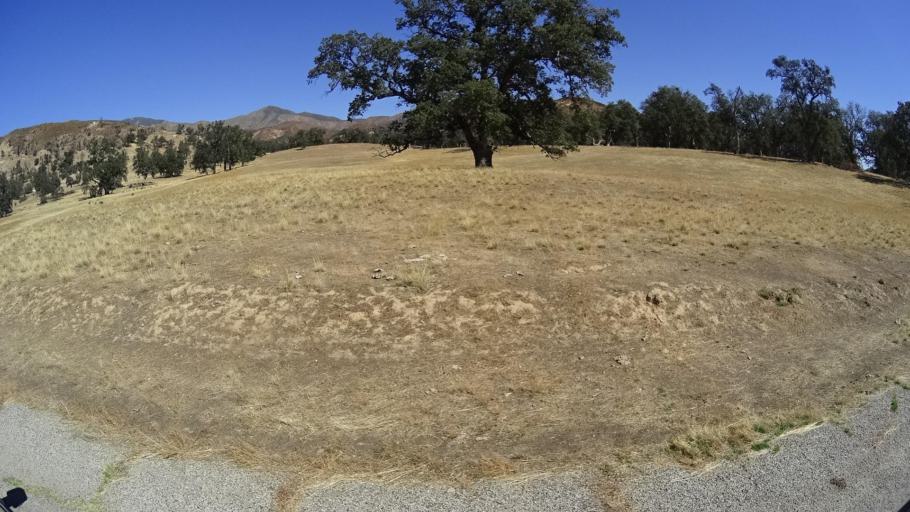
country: US
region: California
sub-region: Monterey County
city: Greenfield
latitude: 36.0845
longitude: -121.4018
